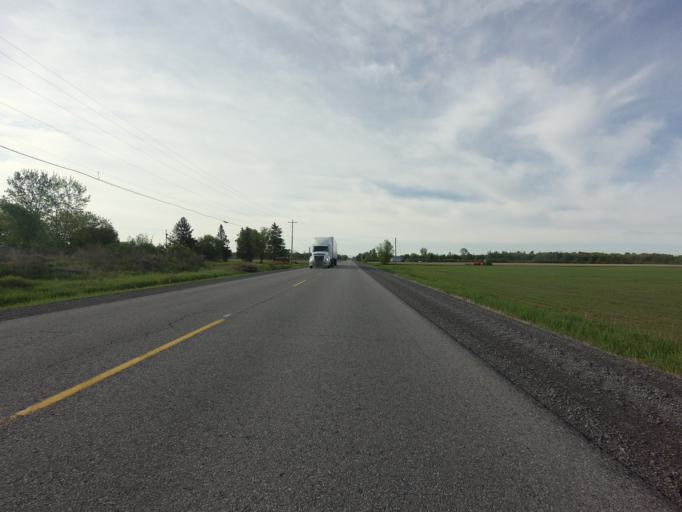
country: CA
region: Ontario
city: Ottawa
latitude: 45.2983
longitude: -75.4527
